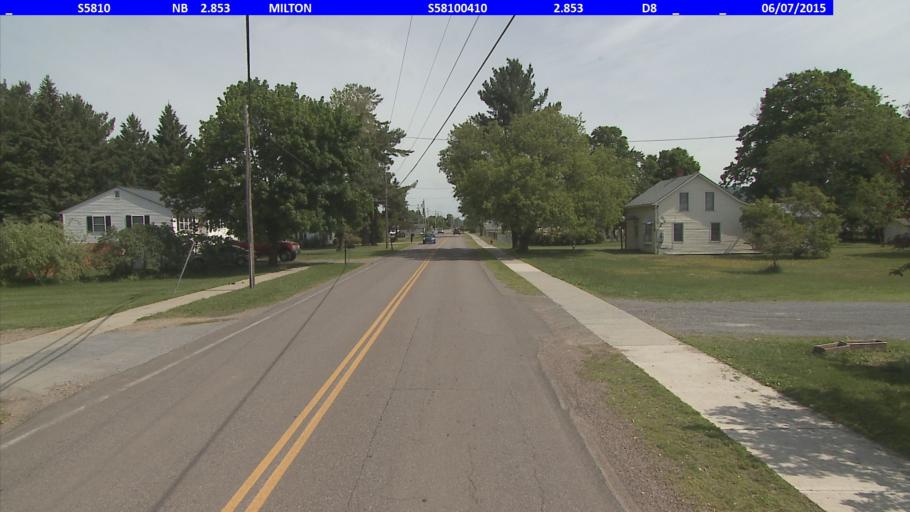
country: US
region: Vermont
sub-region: Chittenden County
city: Milton
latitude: 44.6217
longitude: -73.1190
